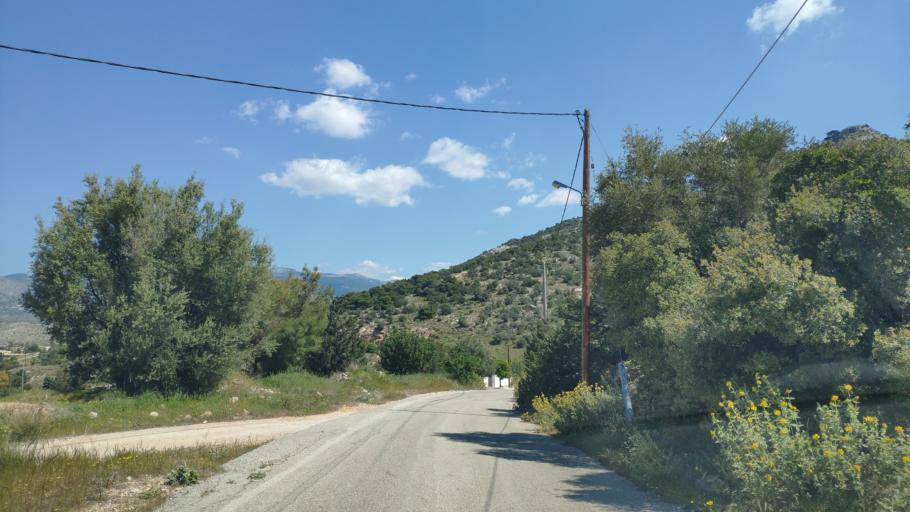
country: GR
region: Attica
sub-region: Nomarchia Athinas
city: Chaidari
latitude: 38.0324
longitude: 23.6358
